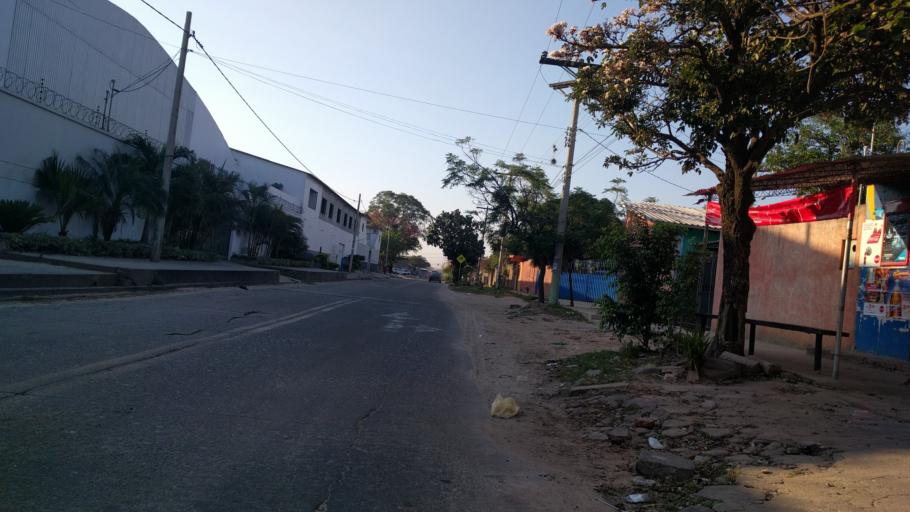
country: BO
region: Santa Cruz
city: Santa Cruz de la Sierra
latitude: -17.8209
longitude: -63.1667
